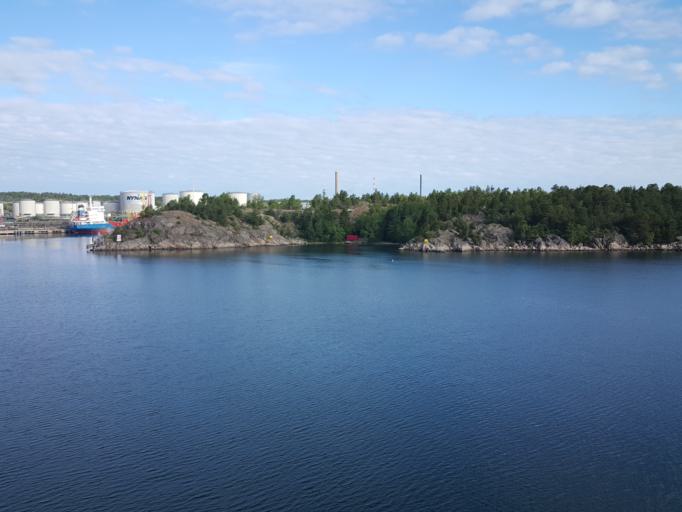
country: SE
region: Stockholm
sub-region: Nynashamns Kommun
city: Nynashamn
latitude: 58.9147
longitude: 17.9782
